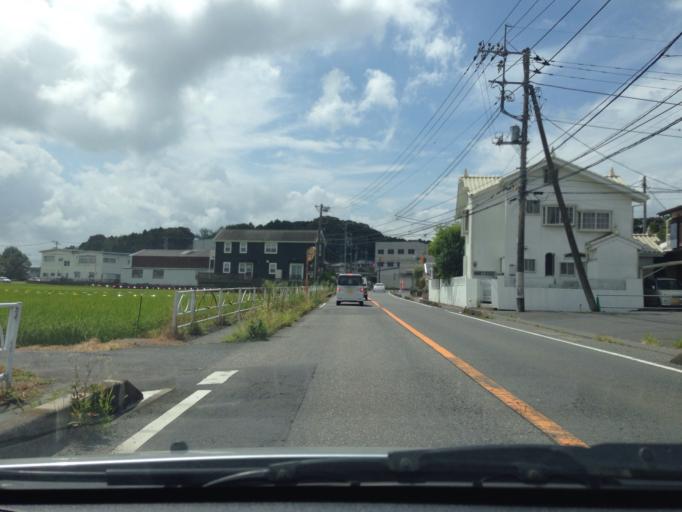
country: JP
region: Ibaraki
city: Ami
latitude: 36.0669
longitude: 140.2106
